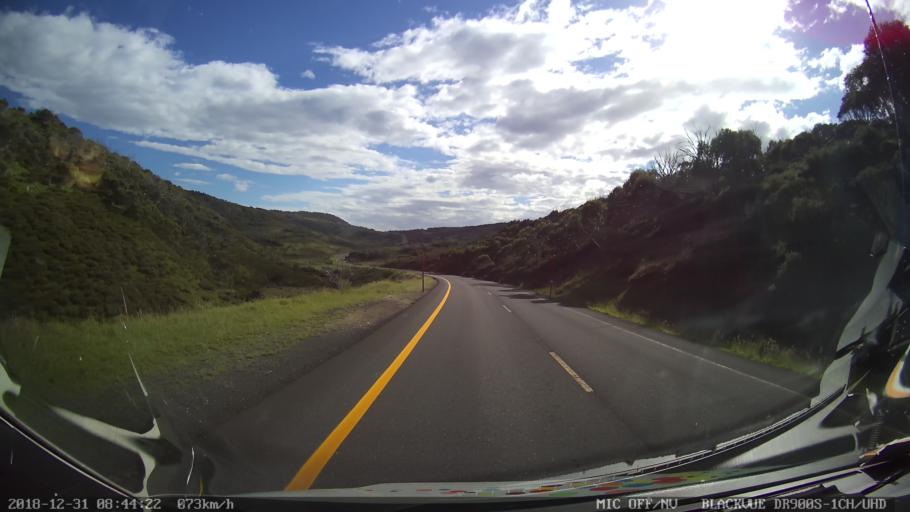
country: AU
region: New South Wales
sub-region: Snowy River
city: Jindabyne
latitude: -36.3841
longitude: 148.4535
